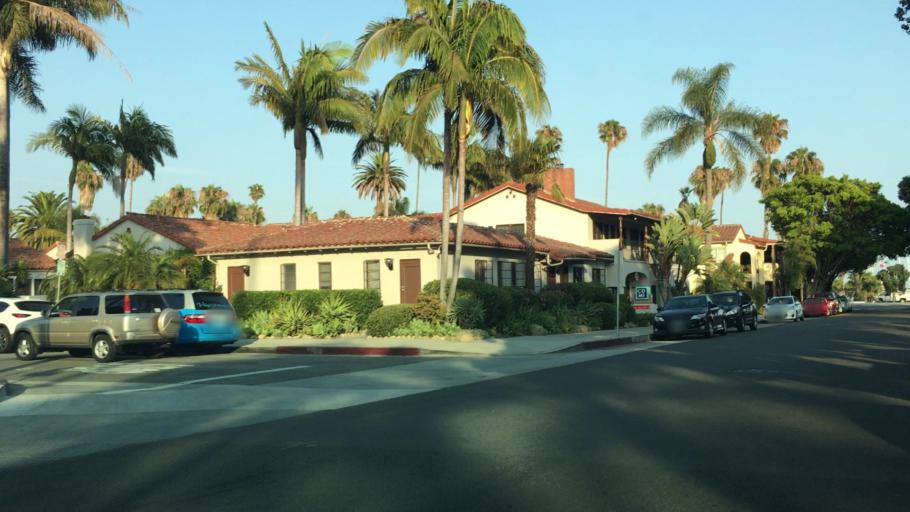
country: US
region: California
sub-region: Santa Barbara County
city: Santa Barbara
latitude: 34.4098
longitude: -119.6938
